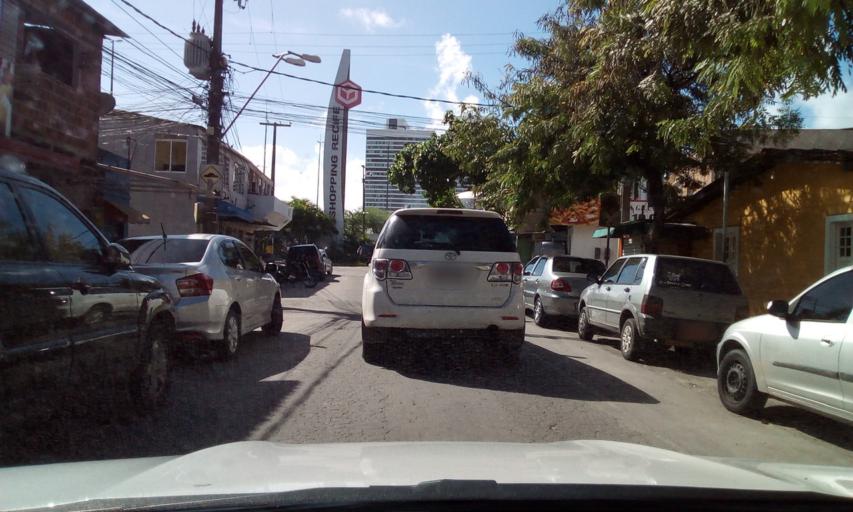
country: BR
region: Pernambuco
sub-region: Recife
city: Recife
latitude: -8.1214
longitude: -34.9040
